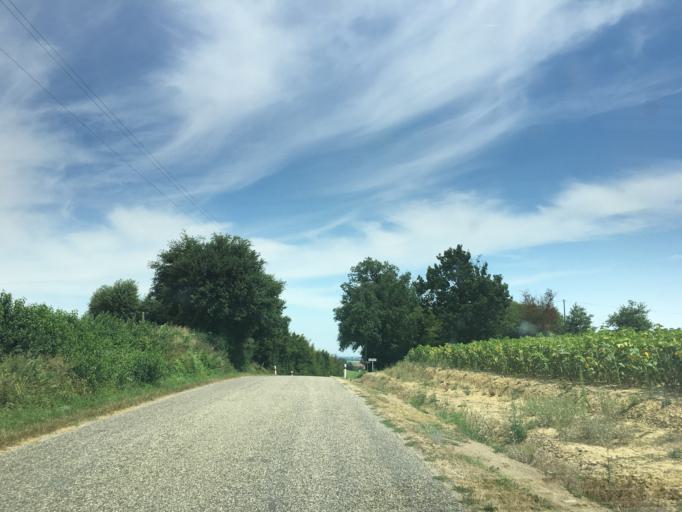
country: FR
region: Midi-Pyrenees
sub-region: Departement du Gers
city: Jegun
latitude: 43.8150
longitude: 0.5301
